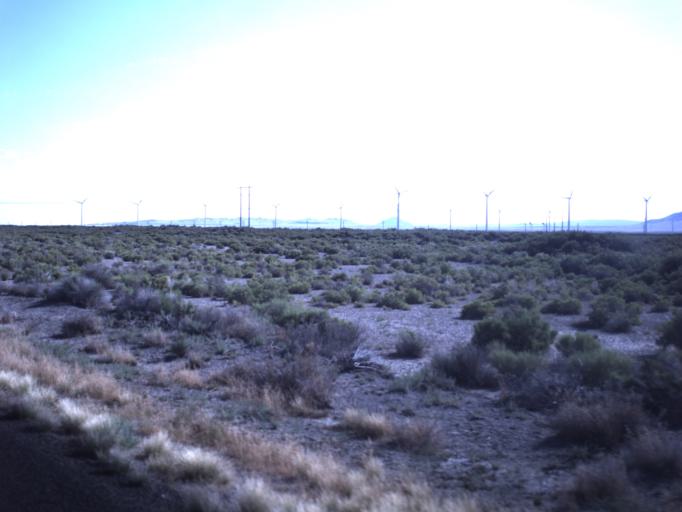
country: US
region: Utah
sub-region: Beaver County
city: Milford
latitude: 38.5681
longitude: -112.9902
